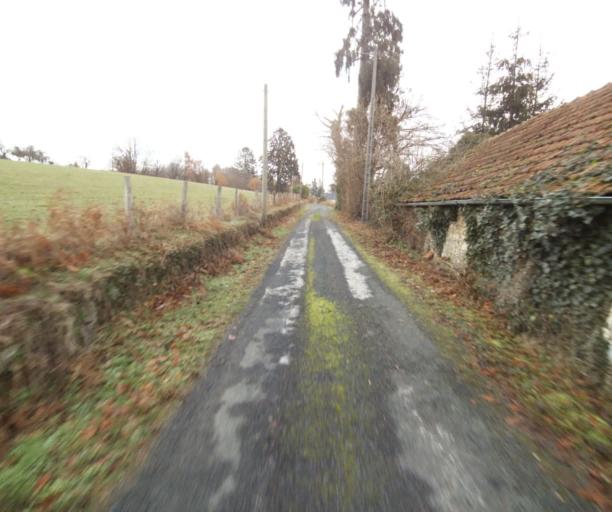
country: FR
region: Limousin
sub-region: Departement de la Correze
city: Chameyrat
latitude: 45.2303
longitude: 1.6935
